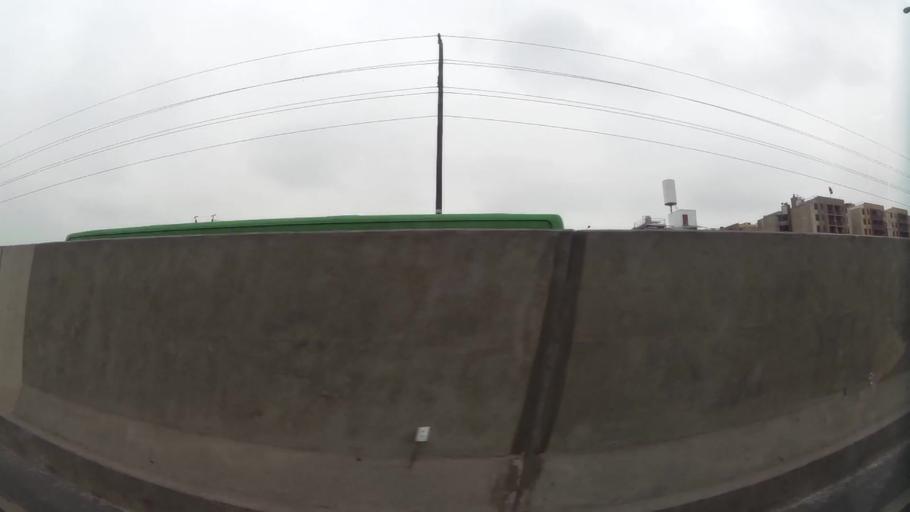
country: PE
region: Lima
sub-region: Lima
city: Independencia
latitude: -11.9500
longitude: -77.0704
